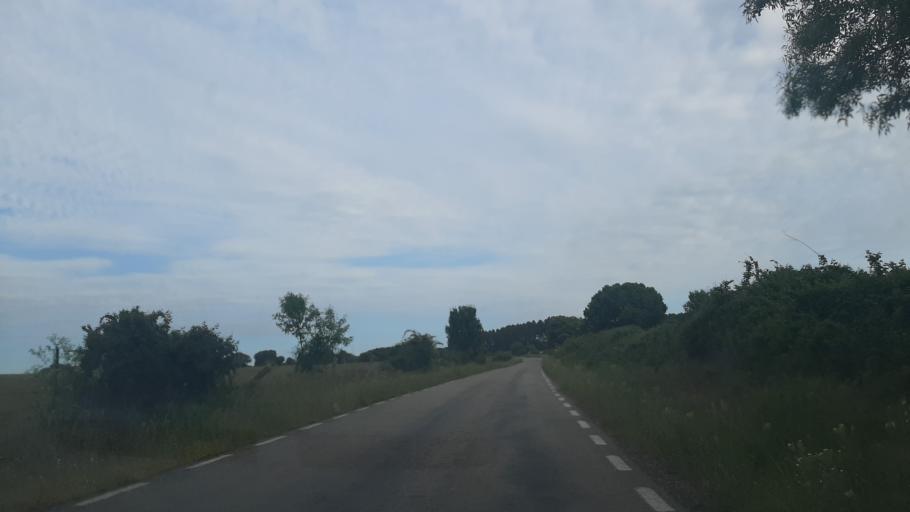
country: ES
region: Castille and Leon
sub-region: Provincia de Salamanca
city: Gallegos de Arganan
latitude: 40.6396
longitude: -6.7296
